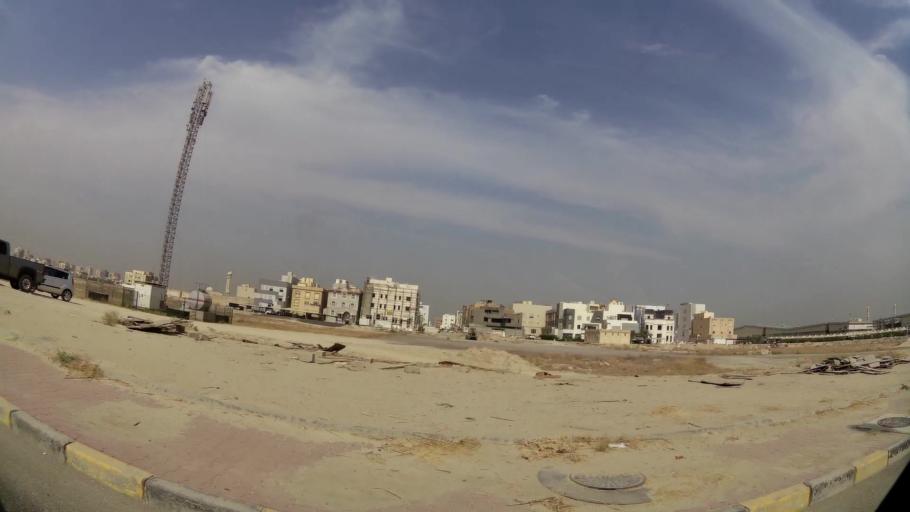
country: KW
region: Al Farwaniyah
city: Janub as Surrah
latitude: 29.2893
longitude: 47.9889
